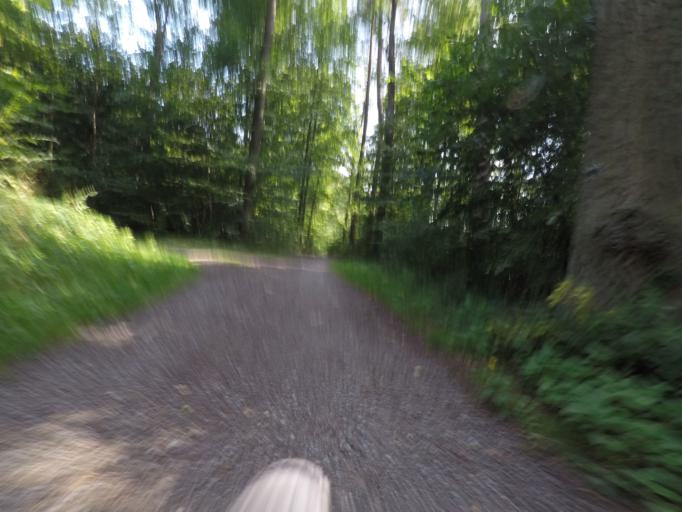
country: DE
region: Baden-Wuerttemberg
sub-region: Regierungsbezirk Stuttgart
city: Steinenbronn
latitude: 48.6983
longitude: 9.1062
